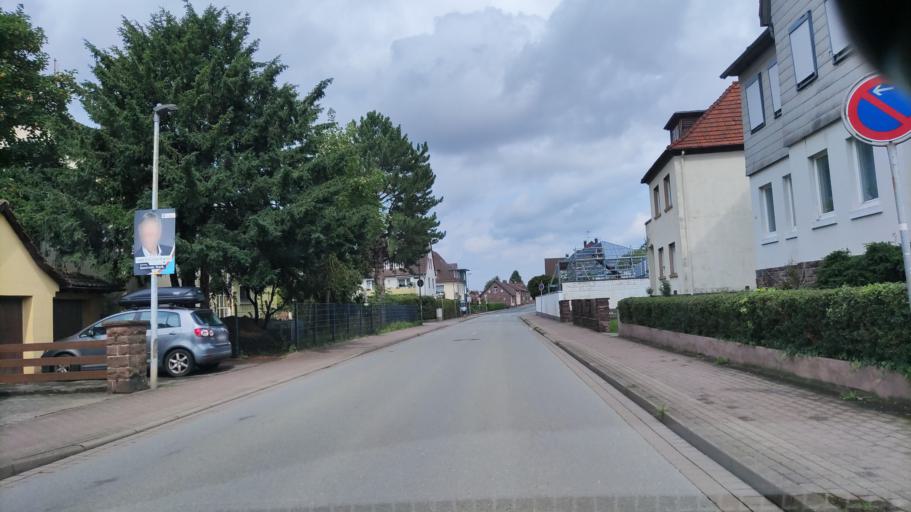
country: DE
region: Lower Saxony
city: Holzminden
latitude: 51.8266
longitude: 9.4675
